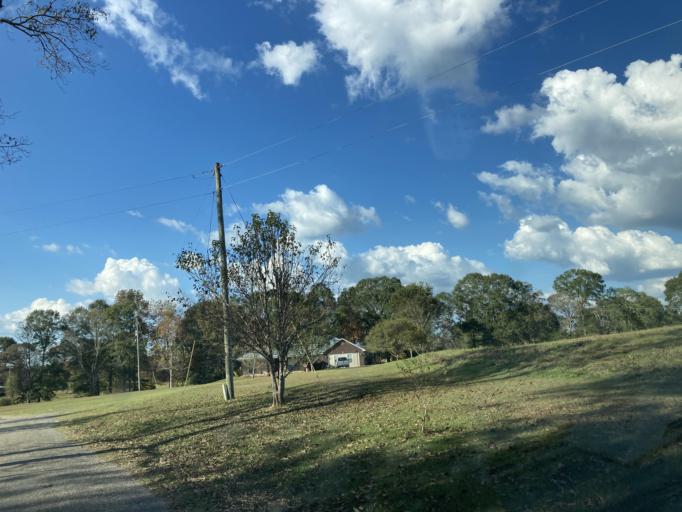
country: US
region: Mississippi
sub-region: Lamar County
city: Sumrall
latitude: 31.4287
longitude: -89.6393
